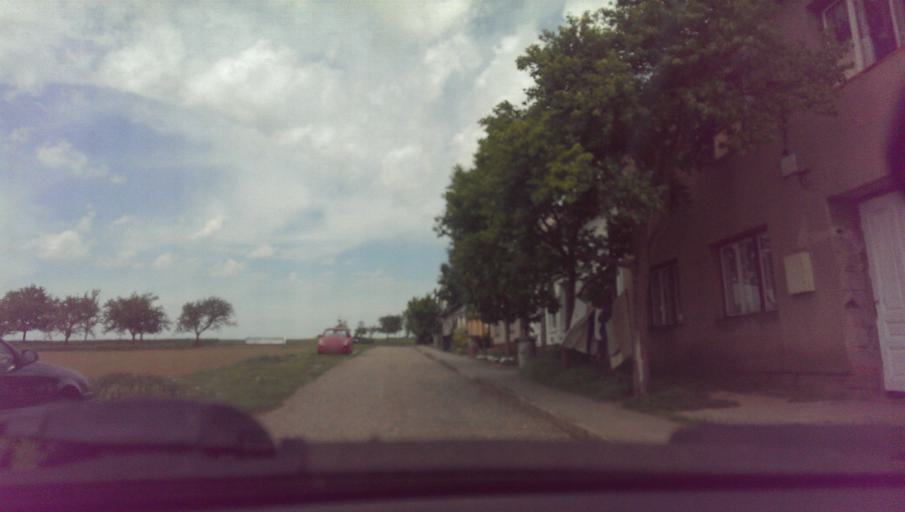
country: CZ
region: Zlin
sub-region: Okres Zlin
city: Otrokovice
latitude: 49.2516
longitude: 17.5419
